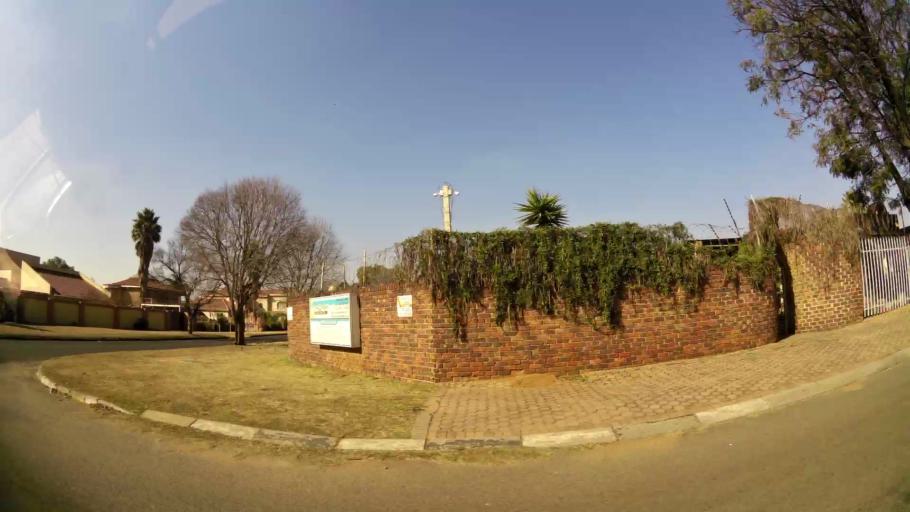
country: ZA
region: Gauteng
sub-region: West Rand District Municipality
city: Randfontein
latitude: -26.1742
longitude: 27.6901
